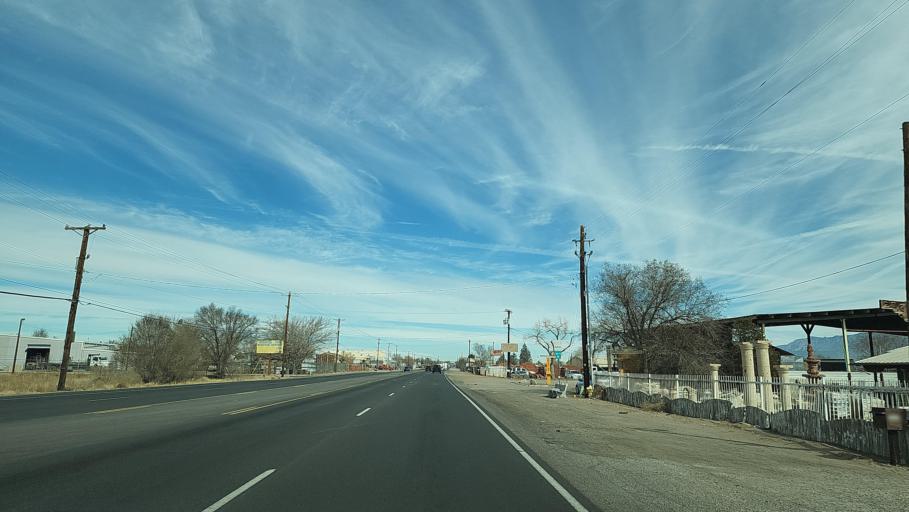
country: US
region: New Mexico
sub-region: Bernalillo County
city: South Valley
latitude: 35.0423
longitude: -106.7106
